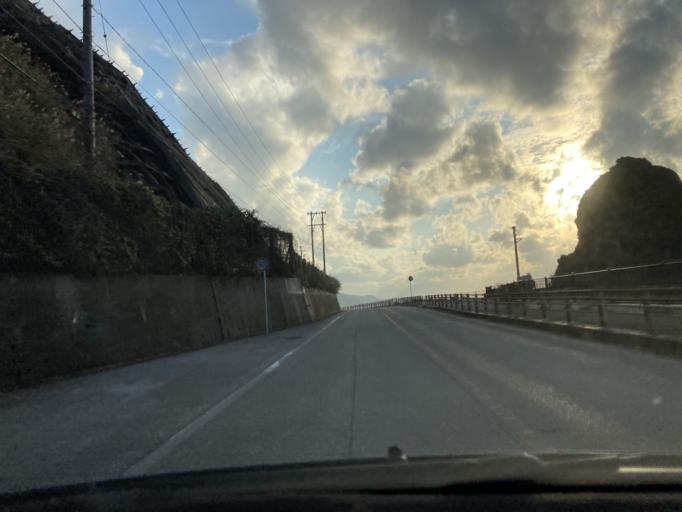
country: JP
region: Okinawa
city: Nago
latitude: 26.8052
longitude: 128.2317
